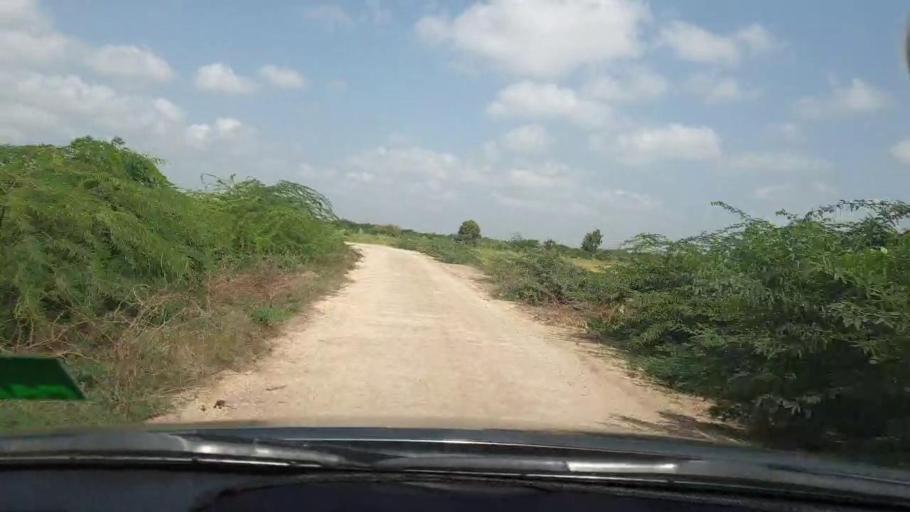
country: PK
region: Sindh
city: Tando Bago
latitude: 24.8715
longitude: 69.0355
